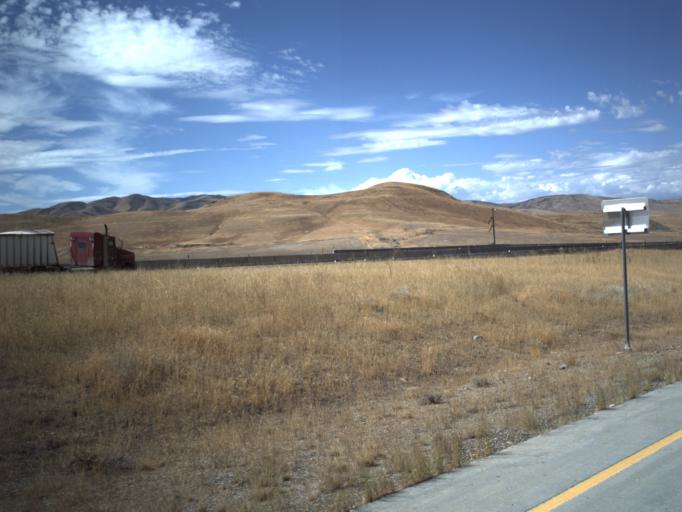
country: US
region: Utah
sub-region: Box Elder County
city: Garland
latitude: 41.8169
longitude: -112.4106
